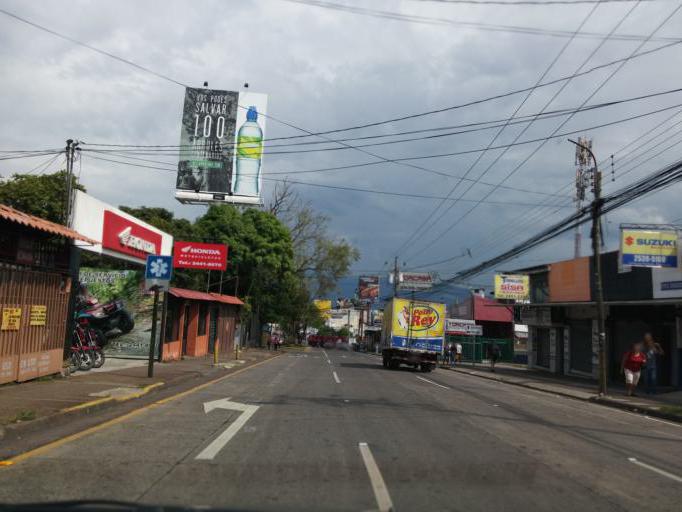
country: CR
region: Alajuela
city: Alajuela
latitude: 10.0109
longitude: -84.2136
